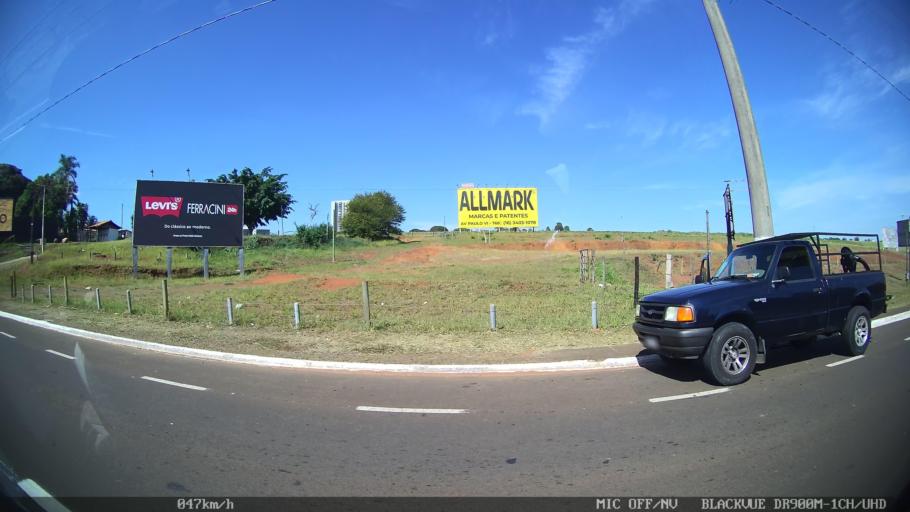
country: BR
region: Sao Paulo
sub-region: Franca
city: Franca
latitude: -20.5550
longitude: -47.4125
